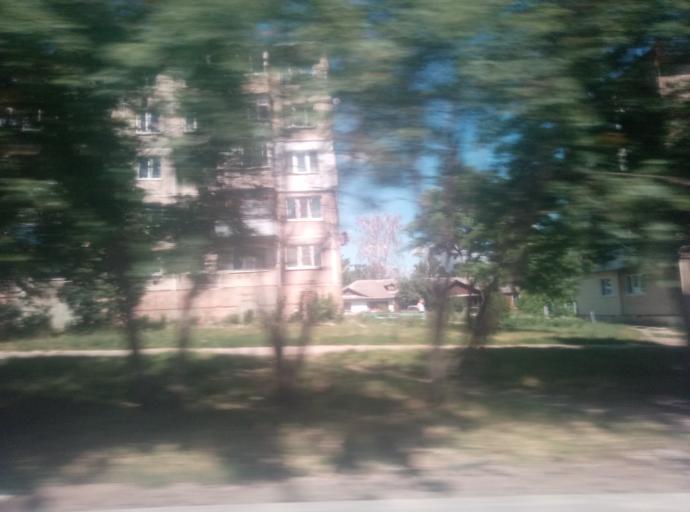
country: RU
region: Tula
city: Kireyevsk
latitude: 53.9232
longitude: 37.9253
